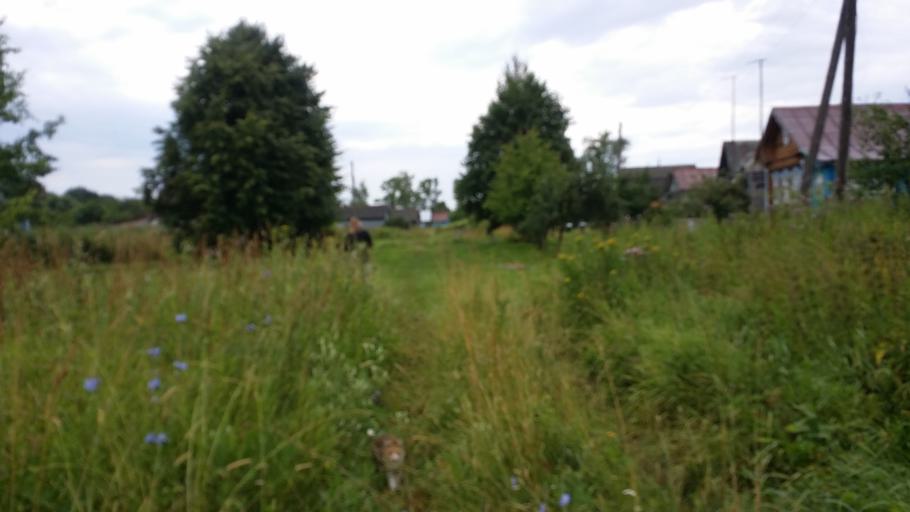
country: RU
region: Vladimir
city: Stavrovo
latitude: 56.3223
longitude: 39.8857
